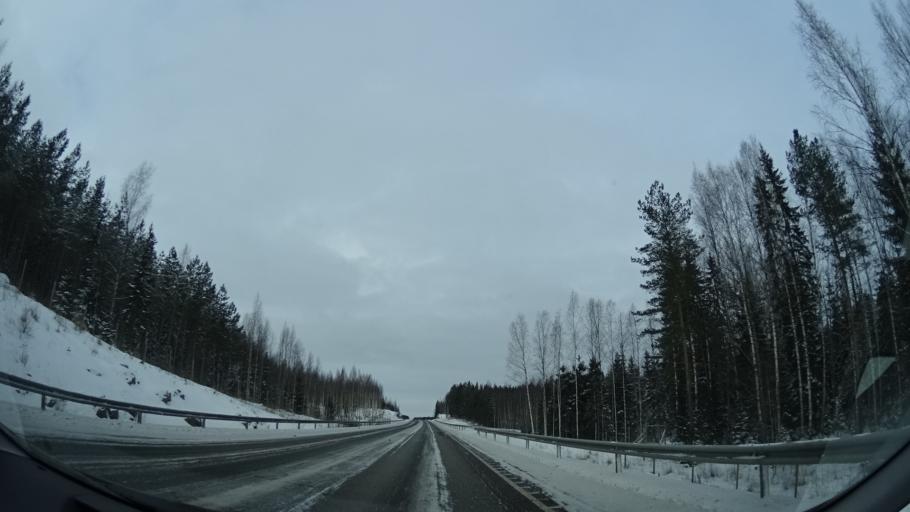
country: FI
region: Uusimaa
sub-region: Helsinki
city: Kaerkoelae
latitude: 60.6195
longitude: 24.0079
